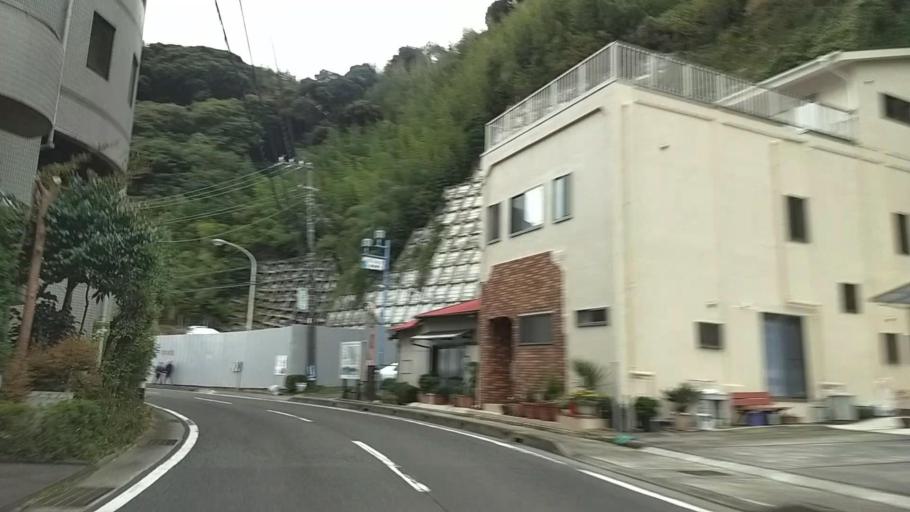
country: JP
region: Kanagawa
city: Yugawara
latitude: 35.1523
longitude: 139.1411
